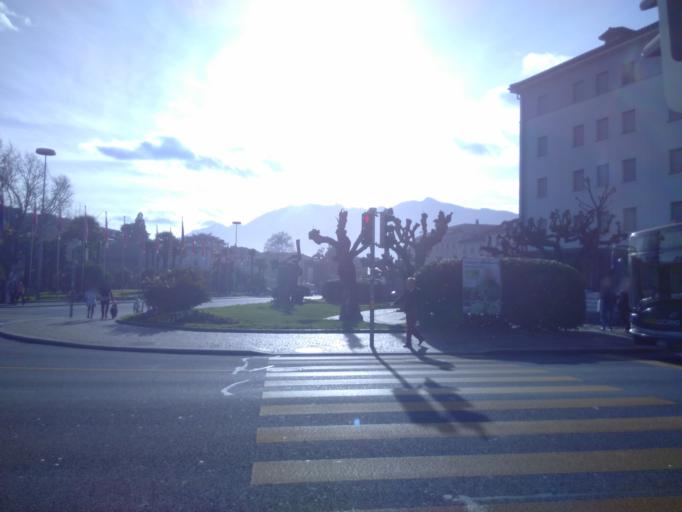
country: CH
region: Ticino
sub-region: Locarno District
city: Locarno
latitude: 46.1704
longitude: 8.8005
